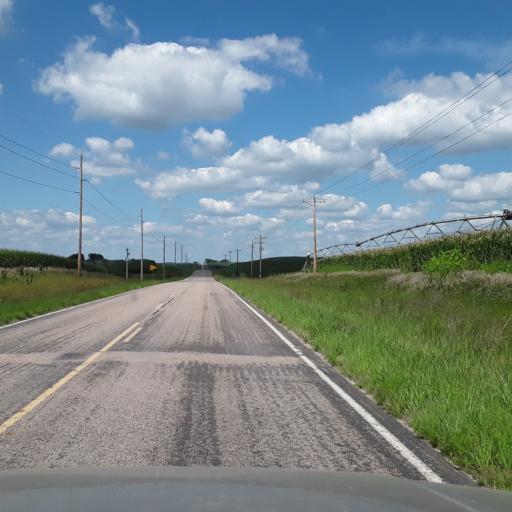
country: US
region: Nebraska
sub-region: Nance County
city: Genoa
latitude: 41.5327
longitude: -97.6960
